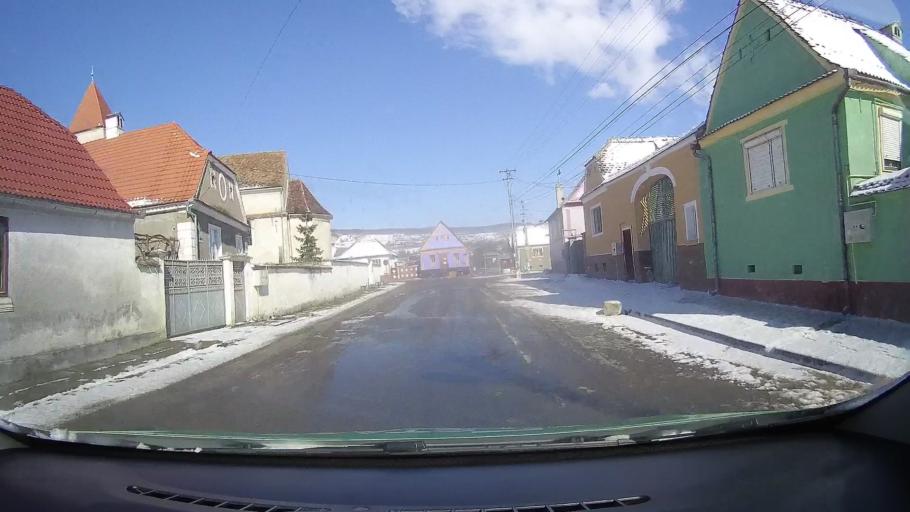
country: RO
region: Sibiu
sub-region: Comuna Avrig
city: Avrig
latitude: 45.7587
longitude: 24.3896
